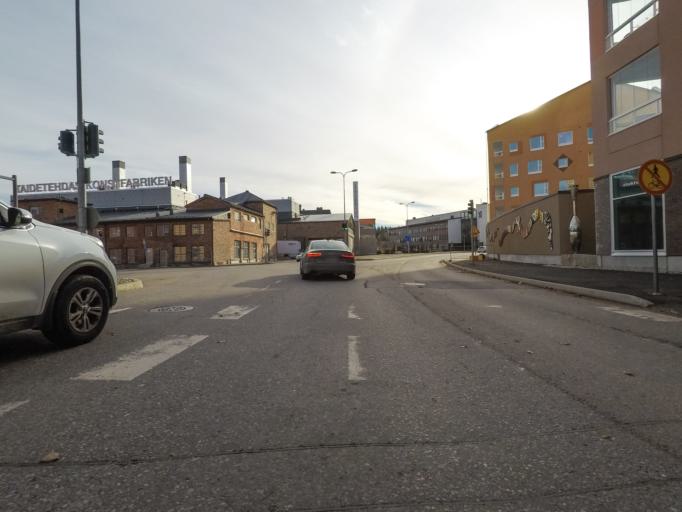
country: FI
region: Uusimaa
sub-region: Porvoo
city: Porvoo
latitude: 60.3891
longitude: 25.6552
